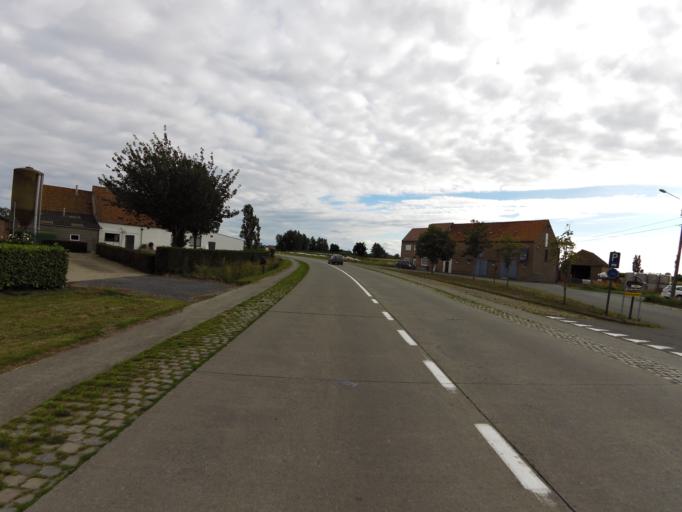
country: BE
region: Flanders
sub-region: Provincie West-Vlaanderen
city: Koekelare
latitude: 51.1154
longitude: 2.9919
